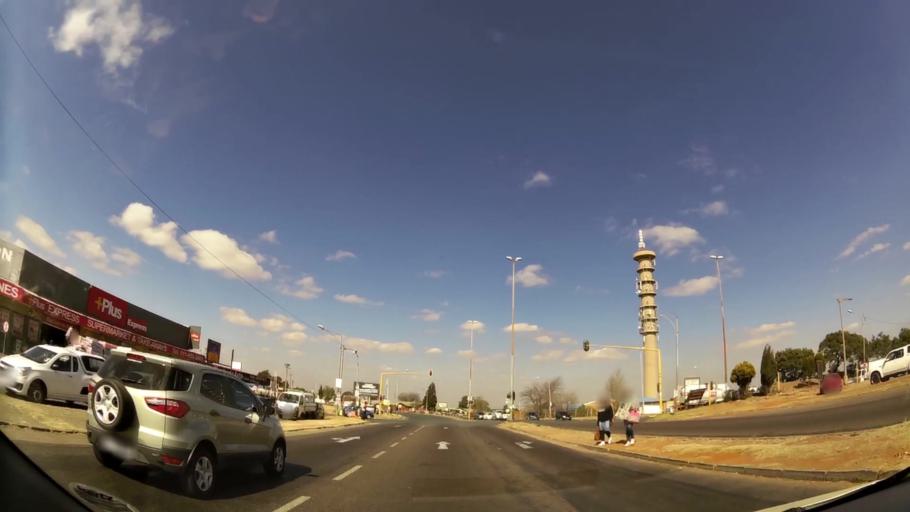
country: ZA
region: Gauteng
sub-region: West Rand District Municipality
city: Krugersdorp
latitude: -26.1194
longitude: 27.8180
